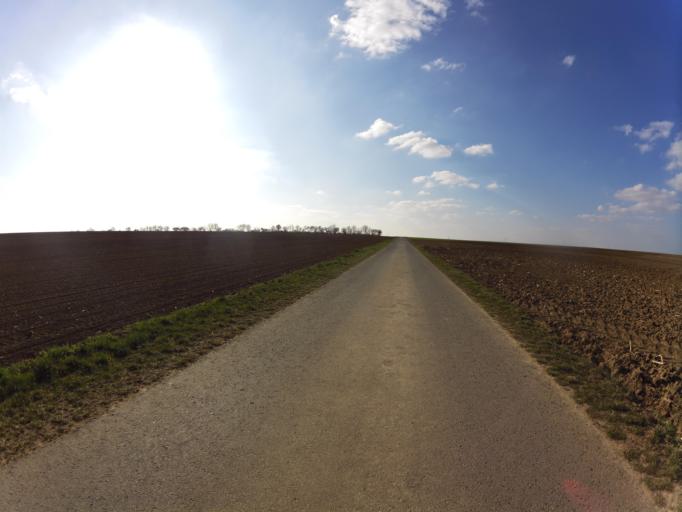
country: DE
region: Bavaria
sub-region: Regierungsbezirk Unterfranken
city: Prosselsheim
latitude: 49.8415
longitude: 10.1258
